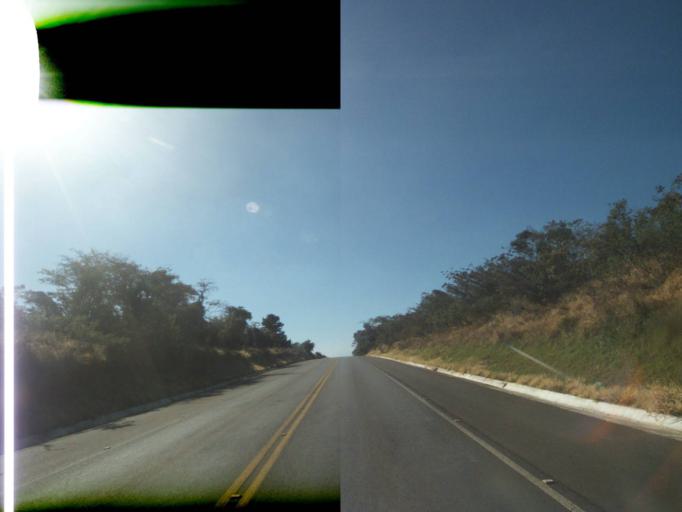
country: BR
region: Parana
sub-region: Tibagi
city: Tibagi
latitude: -24.7336
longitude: -50.4533
